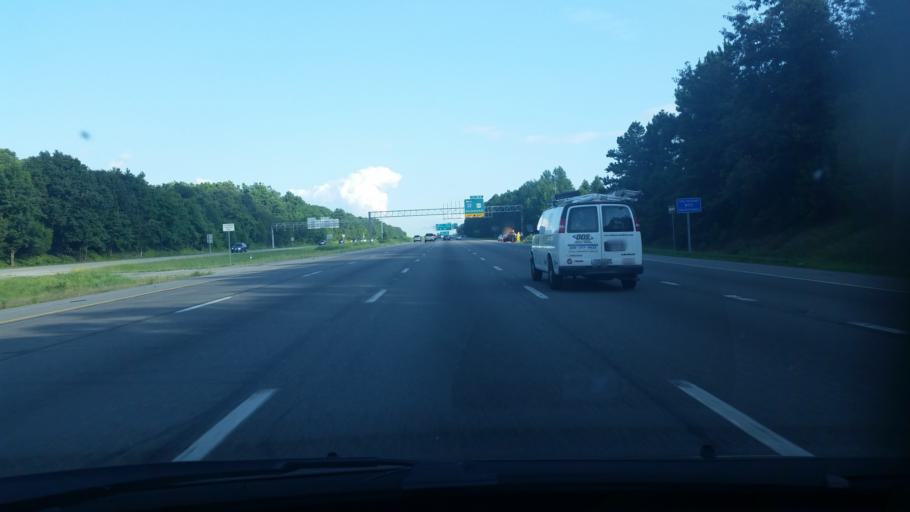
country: US
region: Virginia
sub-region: Henrico County
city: Sandston
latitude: 37.5426
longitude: -77.2818
